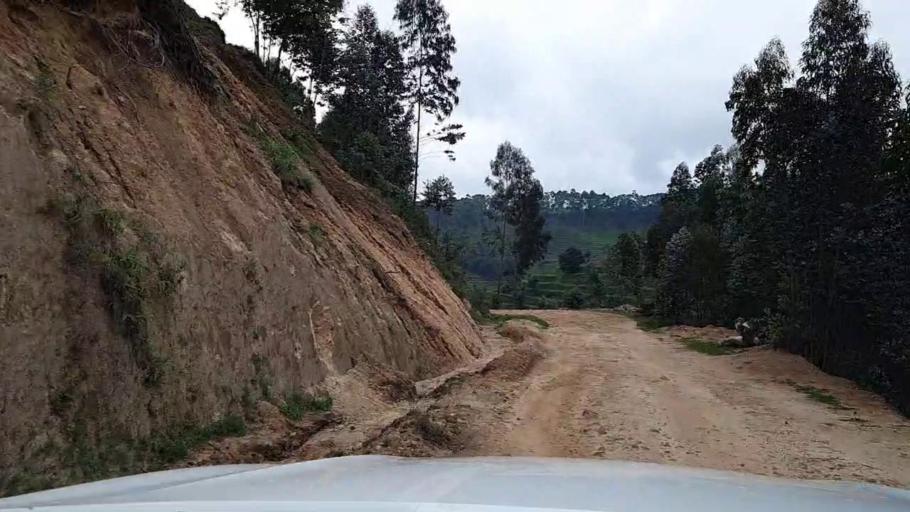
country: RW
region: Western Province
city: Kibuye
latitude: -2.2870
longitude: 29.3692
